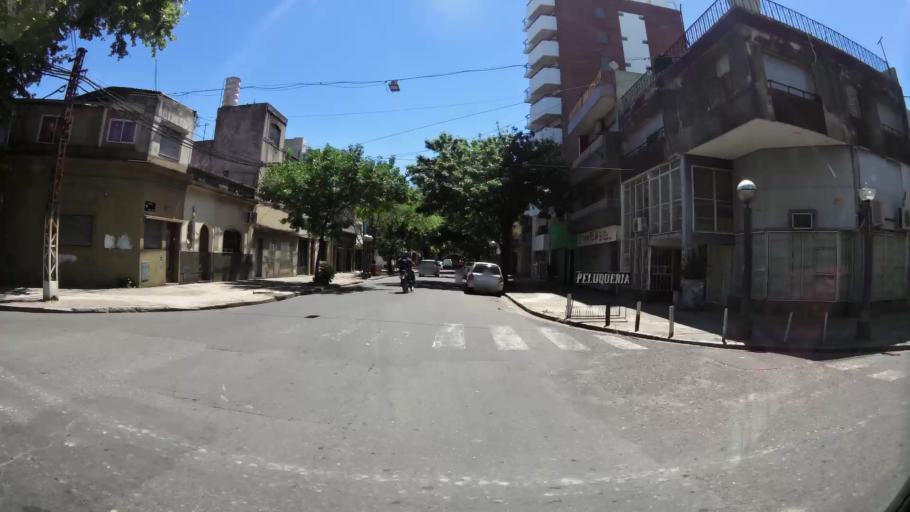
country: AR
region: Santa Fe
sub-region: Departamento de Rosario
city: Rosario
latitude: -32.9372
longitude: -60.6687
